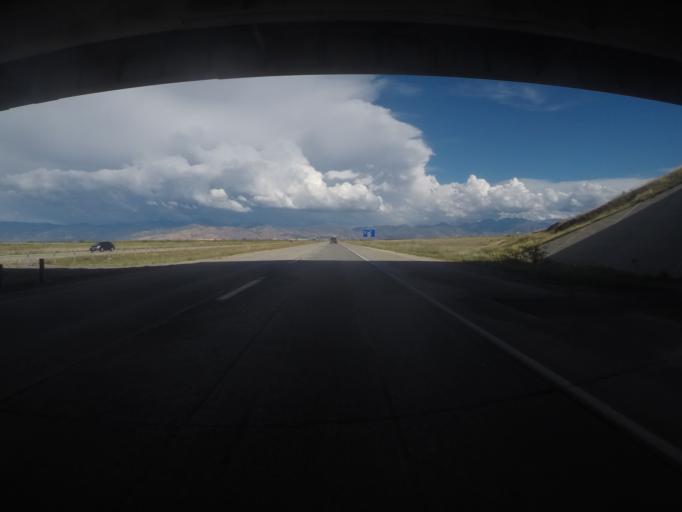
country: US
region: Utah
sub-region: Salt Lake County
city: Magna
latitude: 40.7708
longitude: -112.0630
